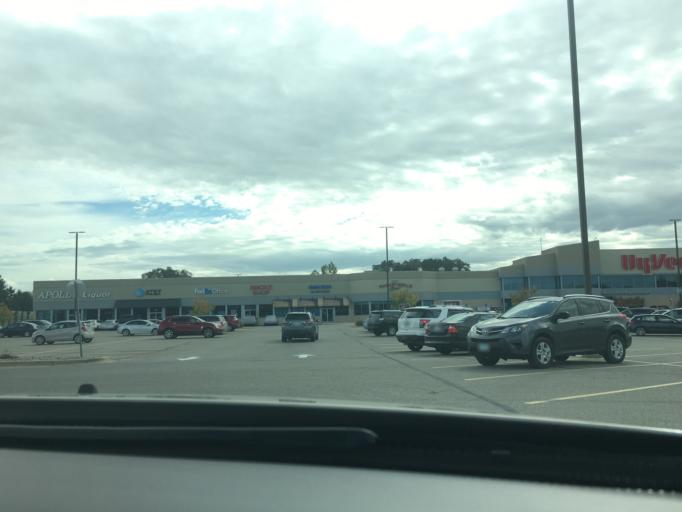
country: US
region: Minnesota
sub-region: Olmsted County
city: Rochester
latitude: 44.0064
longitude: -92.4695
